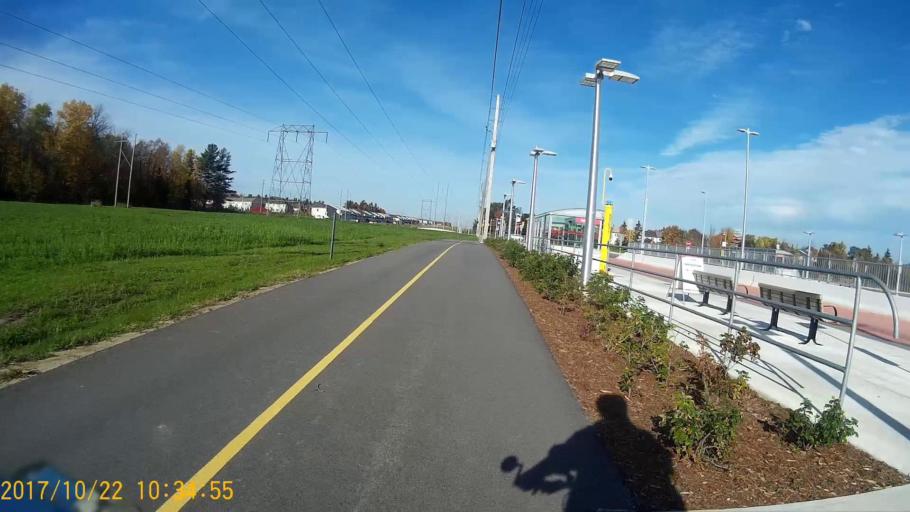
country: CA
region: Ontario
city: Bells Corners
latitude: 45.3428
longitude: -75.9321
